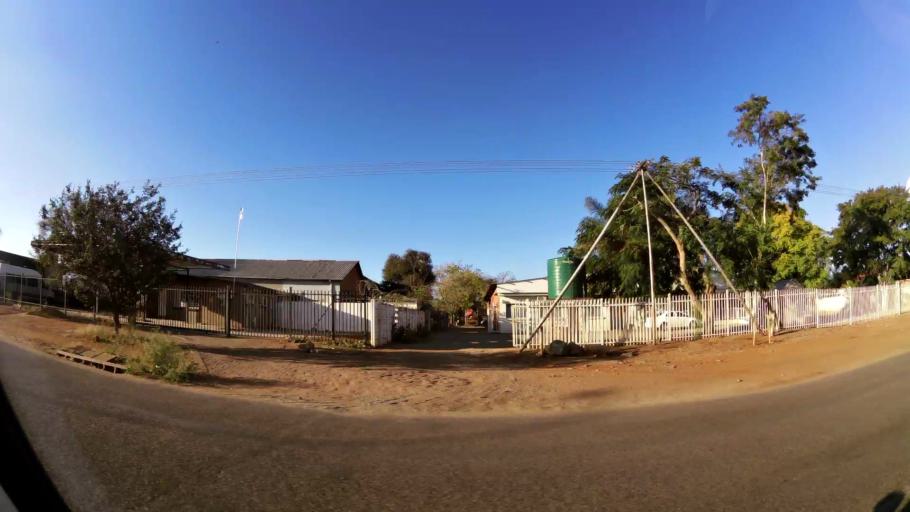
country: ZA
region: Limpopo
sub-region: Waterberg District Municipality
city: Mokopane
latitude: -24.1691
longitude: 28.9973
